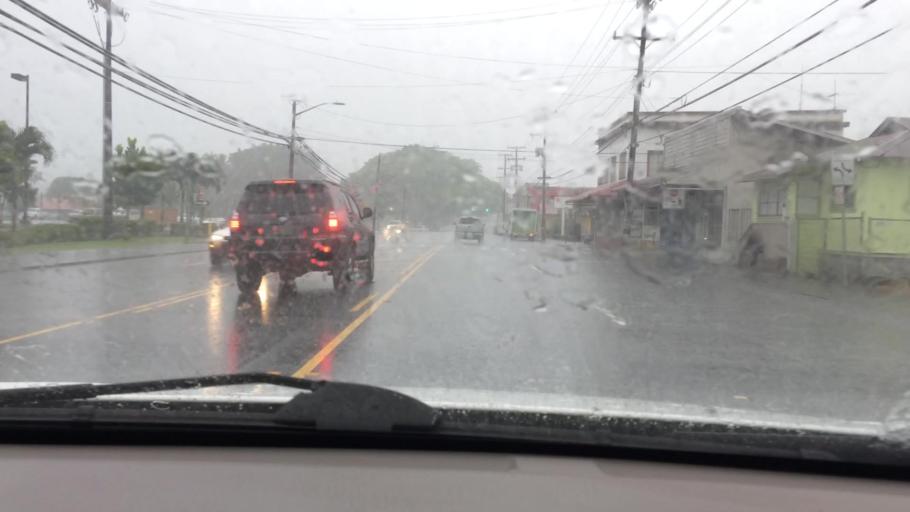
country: US
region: Hawaii
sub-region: Hawaii County
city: Hilo
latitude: 19.7174
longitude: -155.0798
